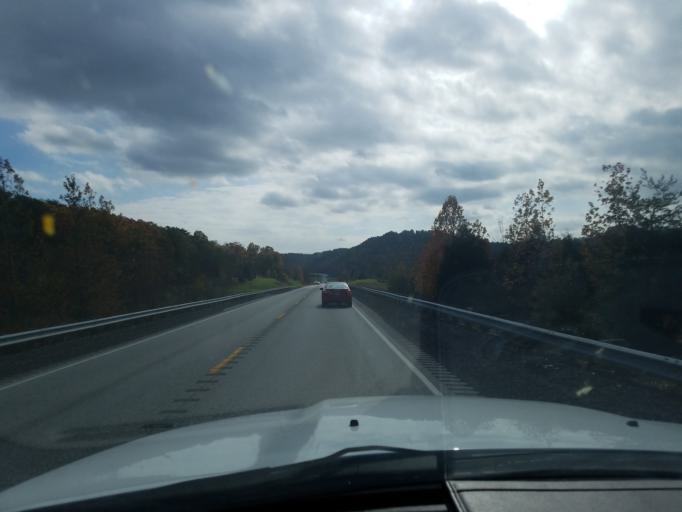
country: US
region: Kentucky
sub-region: Marion County
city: Lebanon
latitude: 37.4645
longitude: -85.2979
